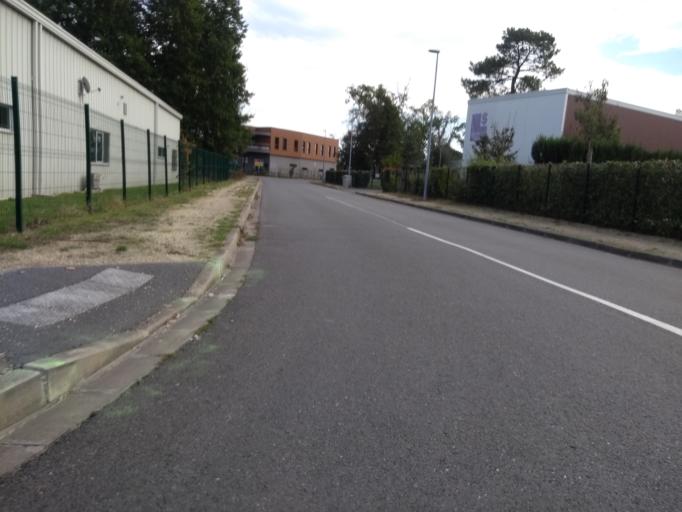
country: FR
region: Aquitaine
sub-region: Departement de la Gironde
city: Canejan
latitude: 44.7726
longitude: -0.6517
